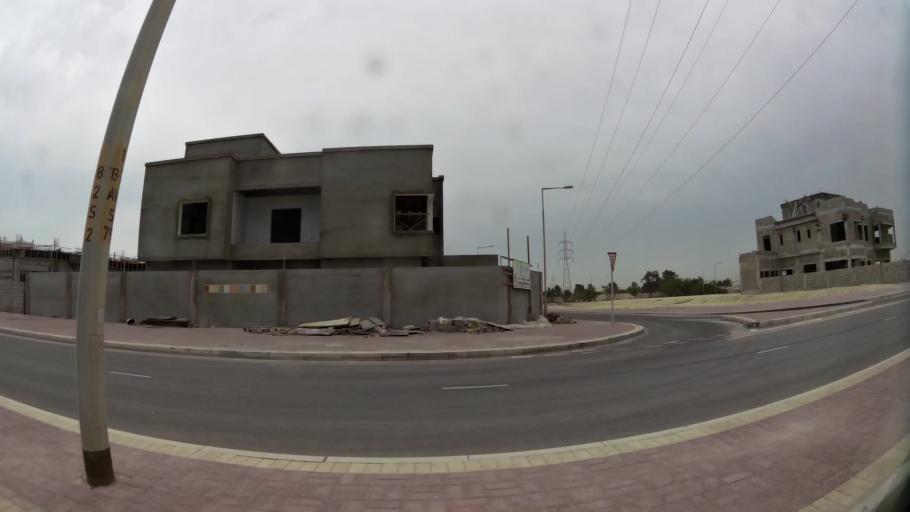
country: BH
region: Northern
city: Madinat `Isa
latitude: 26.1641
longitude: 50.5390
